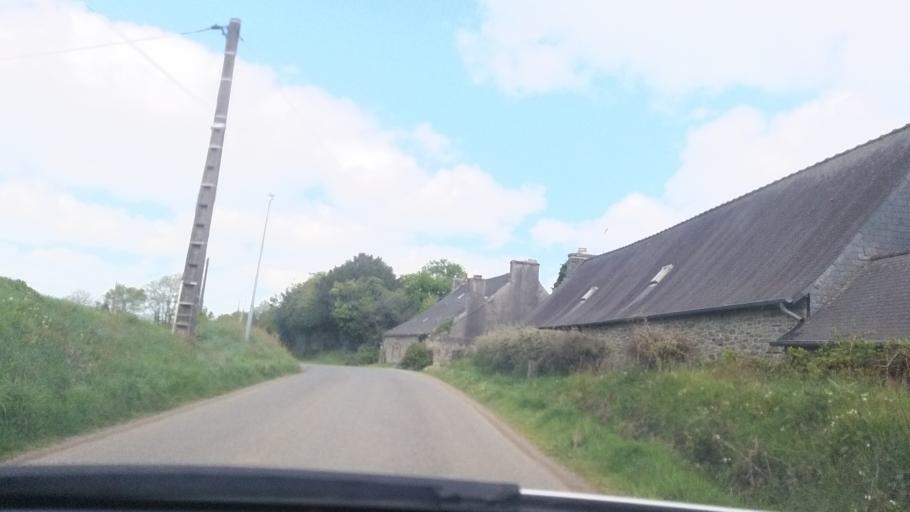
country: FR
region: Brittany
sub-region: Departement du Finistere
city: Huelgoat
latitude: 48.3529
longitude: -3.7176
